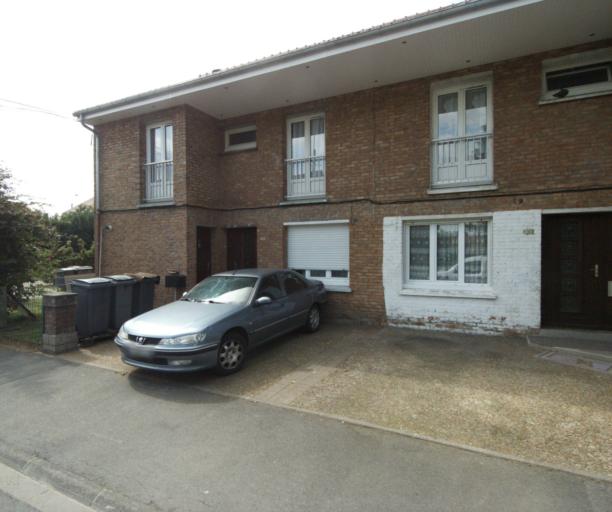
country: FR
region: Nord-Pas-de-Calais
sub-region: Departement du Nord
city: Lannoy
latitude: 50.6633
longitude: 3.1986
